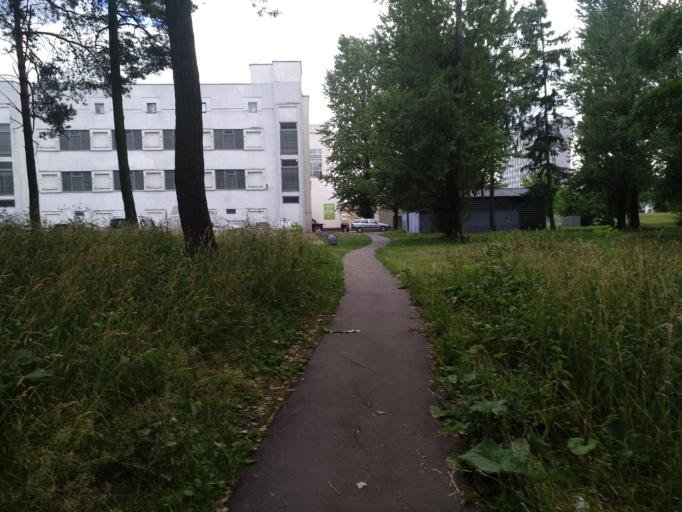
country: BY
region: Minsk
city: Minsk
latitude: 53.8777
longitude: 27.6306
